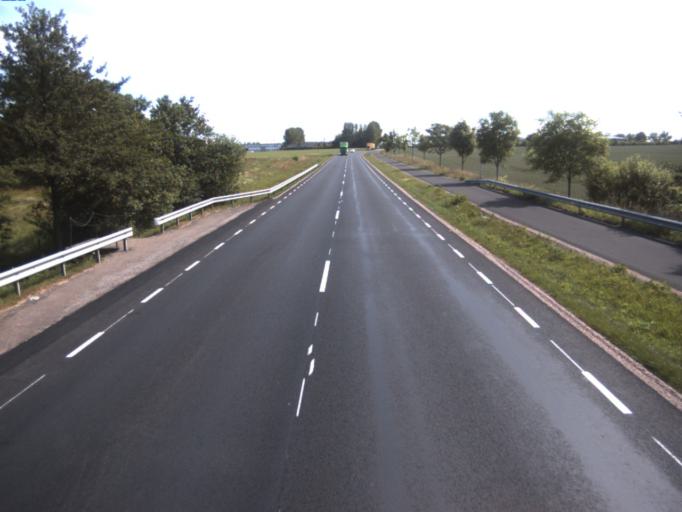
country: SE
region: Skane
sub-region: Helsingborg
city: Barslov
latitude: 56.0423
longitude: 12.7714
